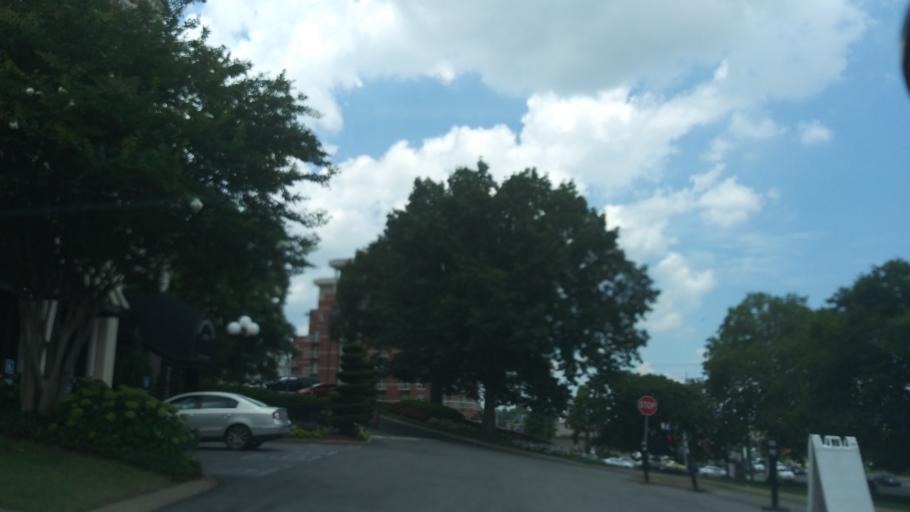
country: US
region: Tennessee
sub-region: Davidson County
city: Nashville
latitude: 36.1422
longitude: -86.8168
